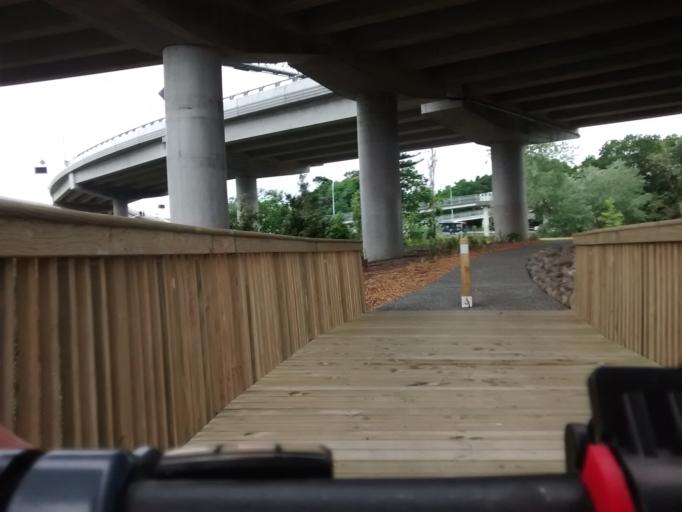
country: NZ
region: Auckland
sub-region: Auckland
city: Rosebank
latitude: -36.8737
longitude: 174.7038
